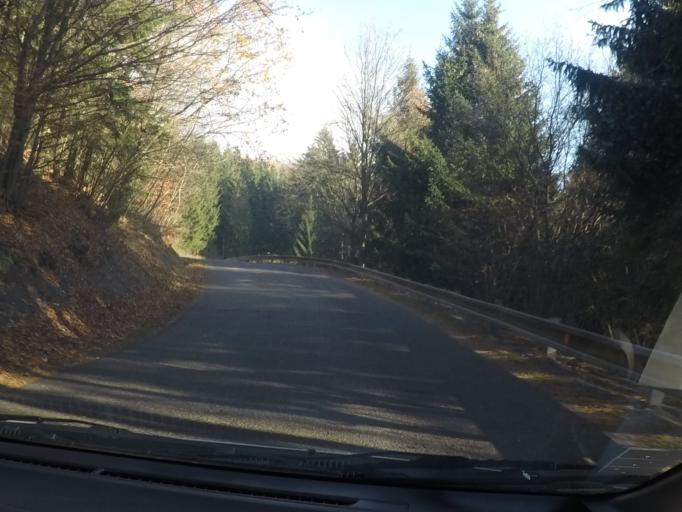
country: SK
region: Banskobystricky
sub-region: Okres Banska Bystrica
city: Banska Stiavnica
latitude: 48.4707
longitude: 18.8692
